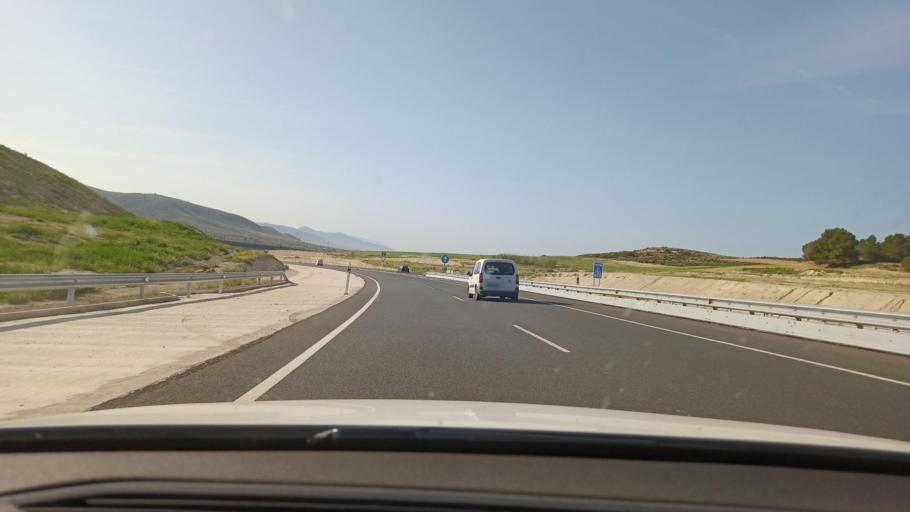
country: ES
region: Castille-La Mancha
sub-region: Provincia de Albacete
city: Caudete
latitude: 38.7231
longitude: -0.9380
